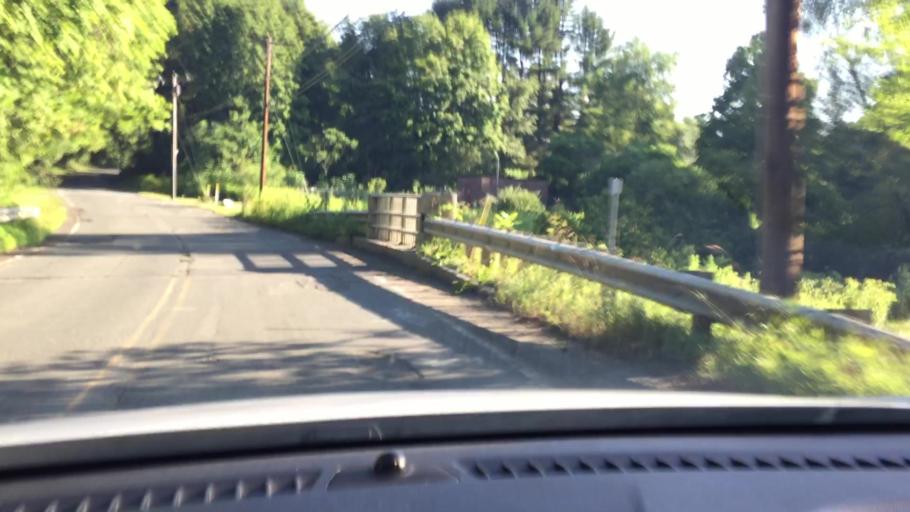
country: US
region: Massachusetts
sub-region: Berkshire County
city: Pittsfield
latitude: 42.4244
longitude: -73.2252
